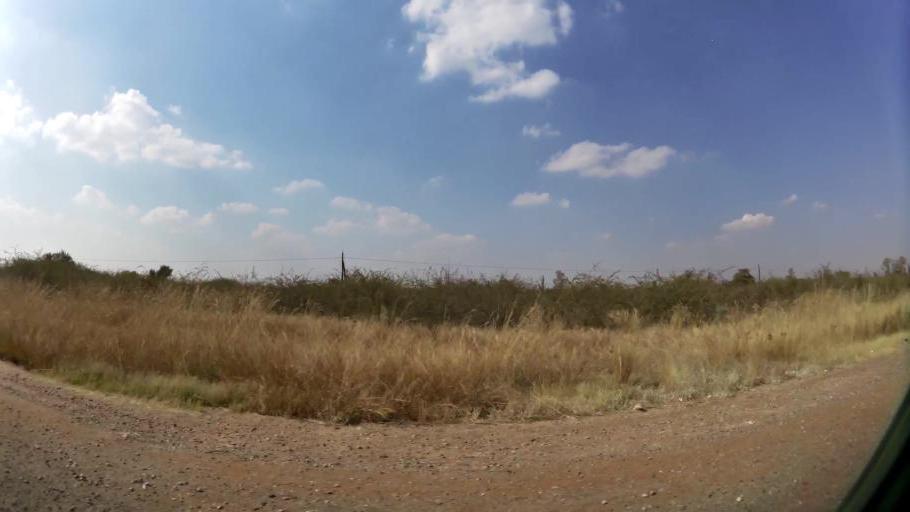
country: ZA
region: North-West
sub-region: Bojanala Platinum District Municipality
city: Rustenburg
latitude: -25.5140
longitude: 27.1006
